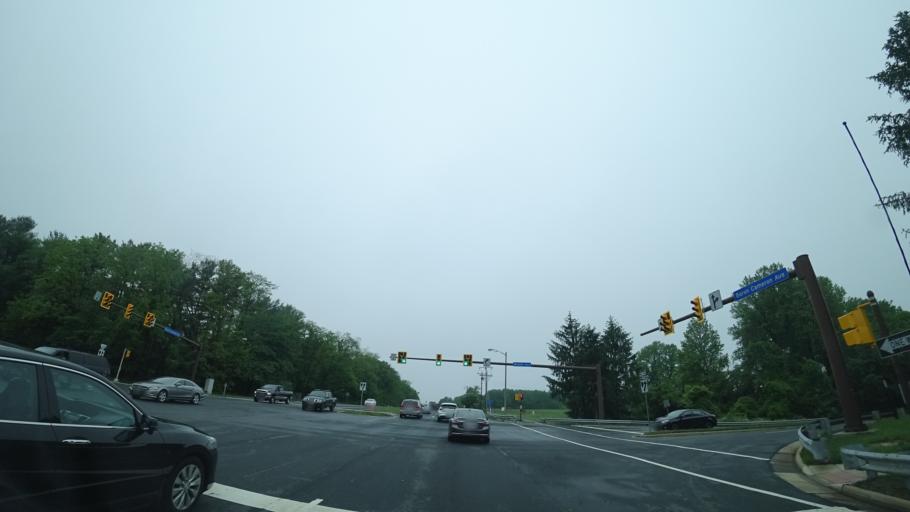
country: US
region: Virginia
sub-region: Fairfax County
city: Reston
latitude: 38.9737
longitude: -77.3333
